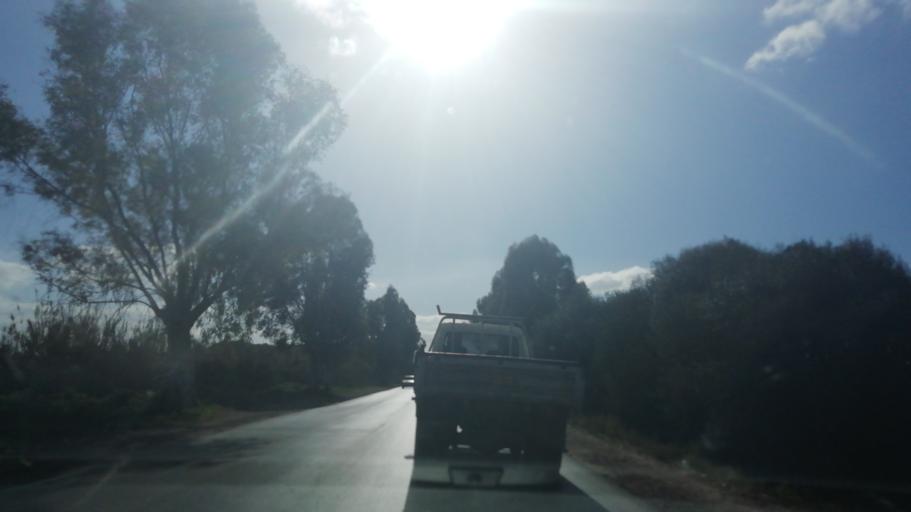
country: DZ
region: Mostaganem
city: Mostaganem
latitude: 35.9795
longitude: 0.2785
